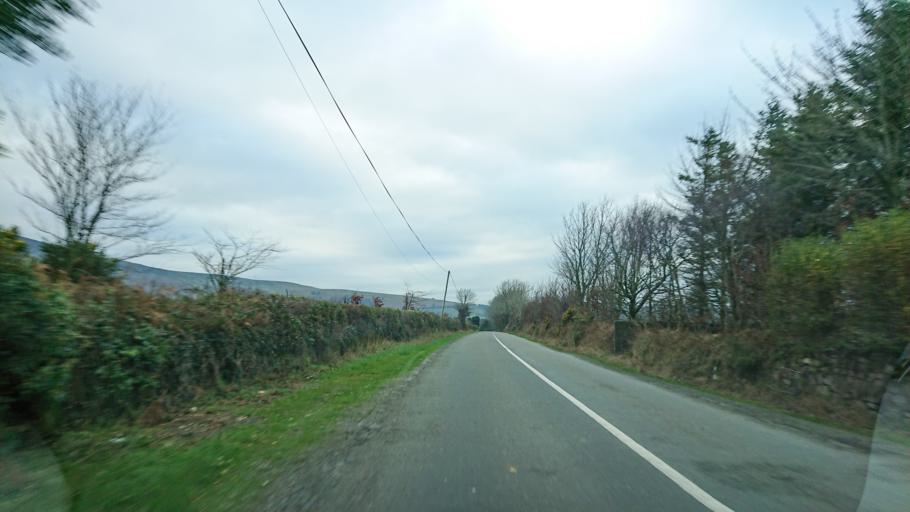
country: IE
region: Munster
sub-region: South Tipperary
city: Cluain Meala
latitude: 52.3209
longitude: -7.5639
